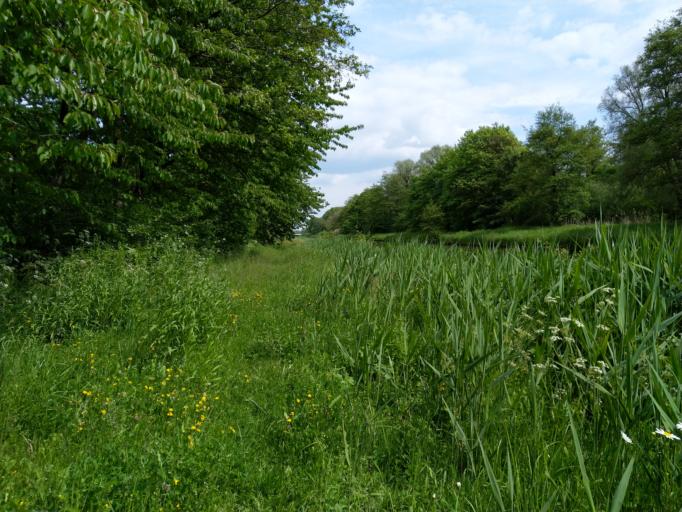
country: FR
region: Picardie
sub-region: Departement de l'Aisne
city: Boue
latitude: 50.0419
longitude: 3.6488
